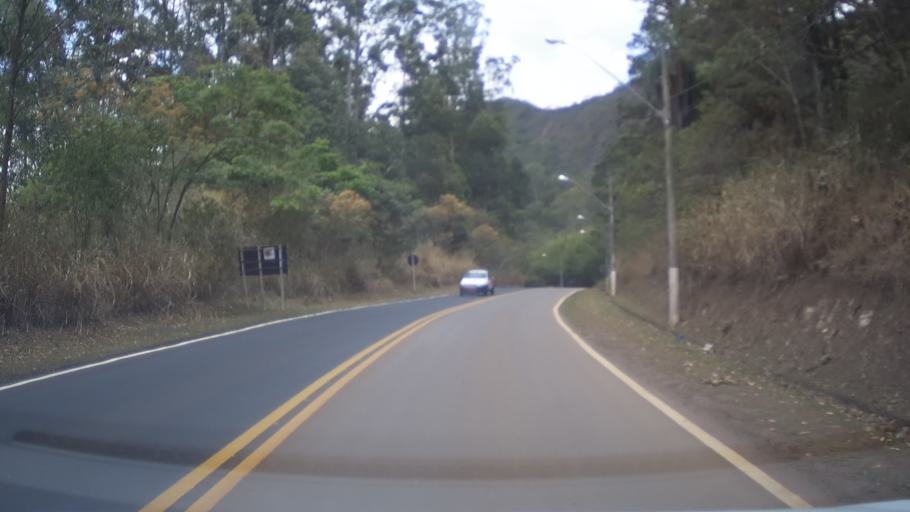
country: BR
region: Minas Gerais
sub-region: Belo Horizonte
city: Belo Horizonte
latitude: -19.9687
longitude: -43.9195
